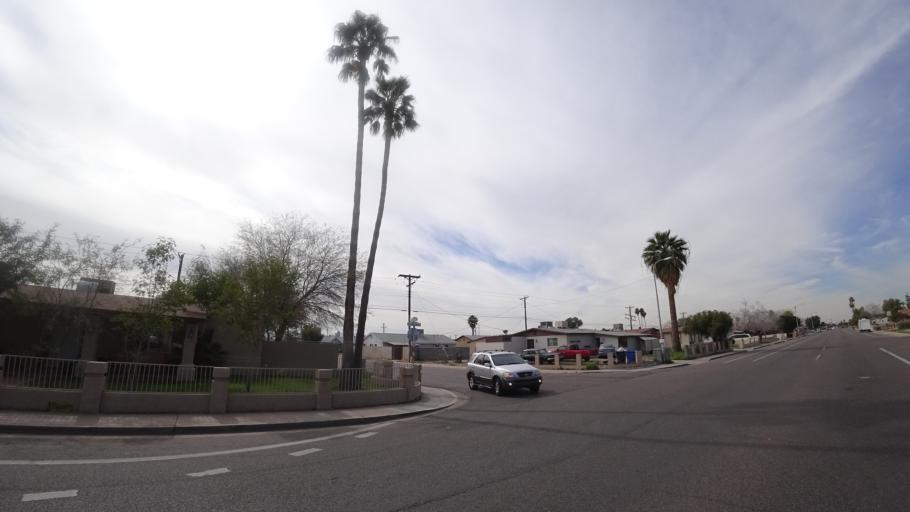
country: US
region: Arizona
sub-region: Maricopa County
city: Glendale
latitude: 33.4878
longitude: -112.1912
